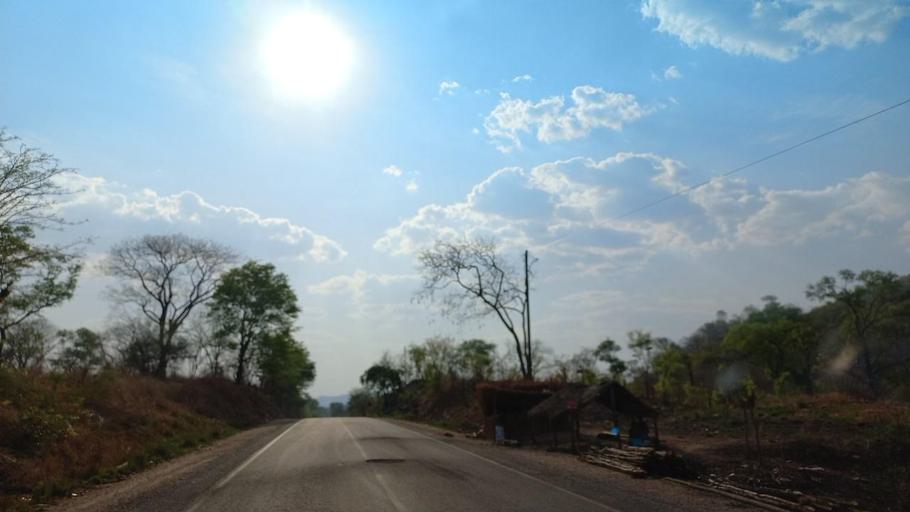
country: ZM
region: Lusaka
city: Luangwa
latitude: -14.9812
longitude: 30.1462
